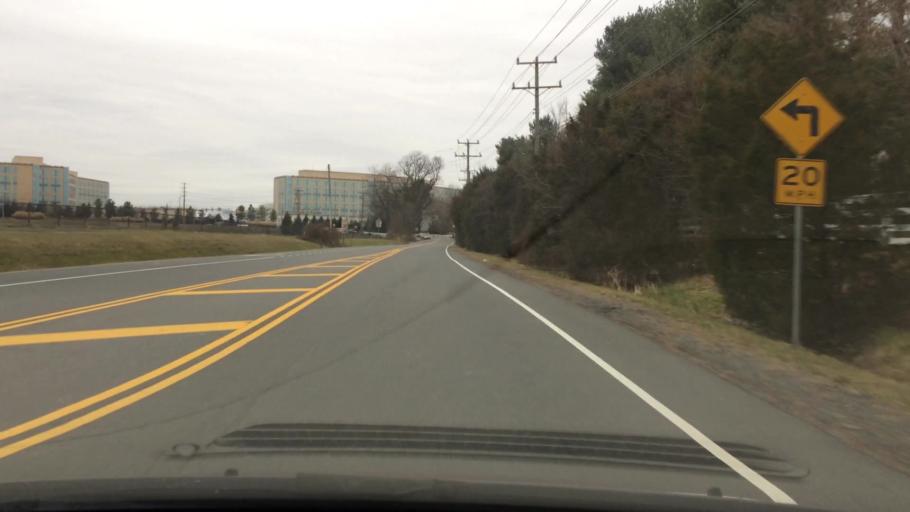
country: US
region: Virginia
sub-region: Fairfax County
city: Chantilly
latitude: 38.9087
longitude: -77.4196
